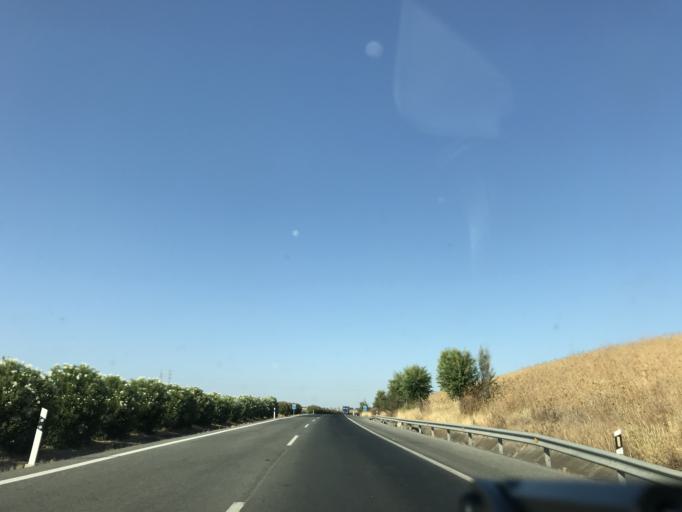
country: ES
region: Andalusia
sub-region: Provincia de Sevilla
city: Ecija
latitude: 37.5382
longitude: -5.0580
